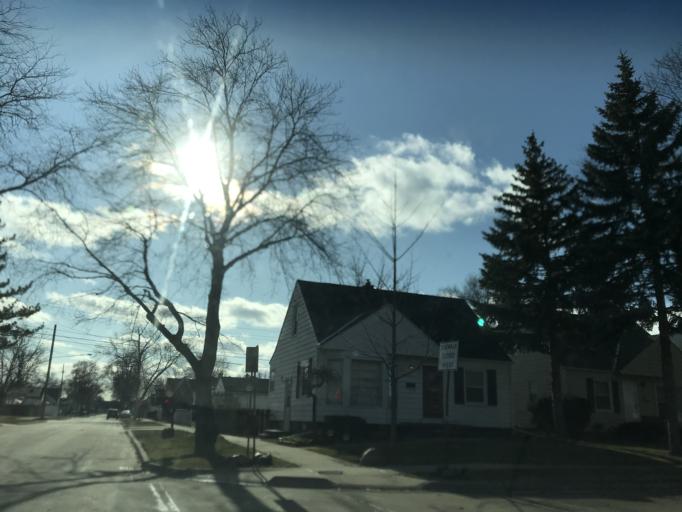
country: US
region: Michigan
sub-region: Oakland County
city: Madison Heights
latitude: 42.4827
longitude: -83.1109
